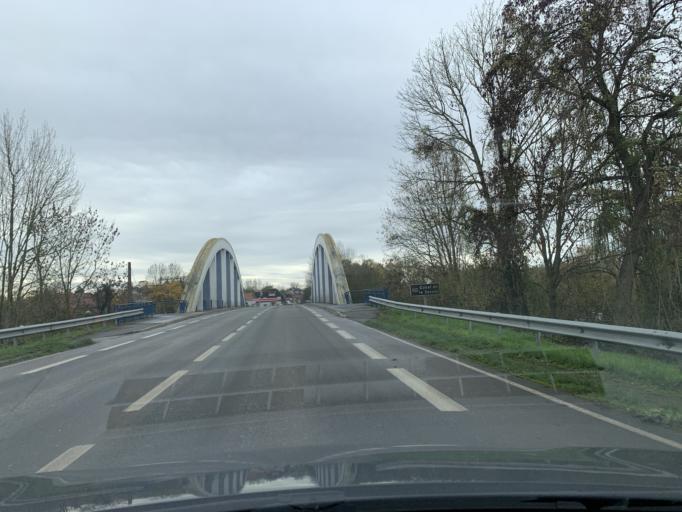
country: FR
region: Nord-Pas-de-Calais
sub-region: Departement du Nord
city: Aubigny-au-Bac
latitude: 50.2600
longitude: 3.1590
